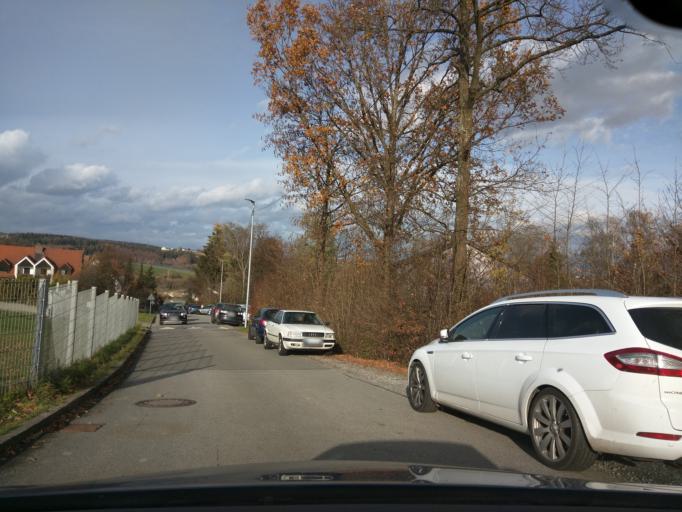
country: DE
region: Bavaria
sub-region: Lower Bavaria
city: Passau
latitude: 48.5664
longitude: 13.4215
